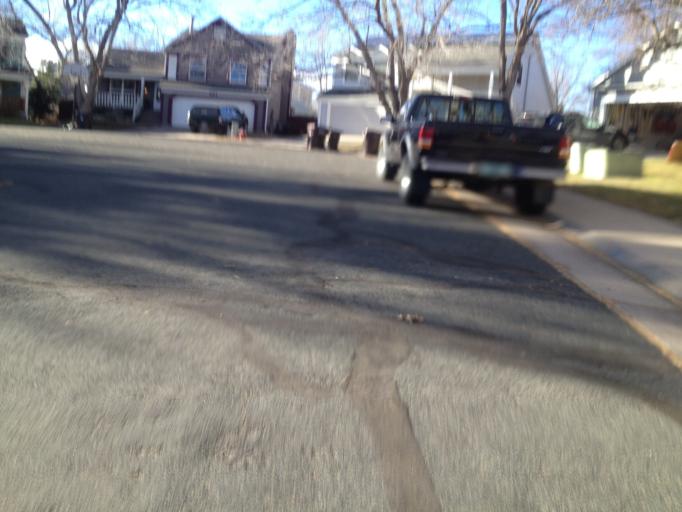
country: US
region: Colorado
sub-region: Boulder County
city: Louisville
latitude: 39.9741
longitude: -105.1523
